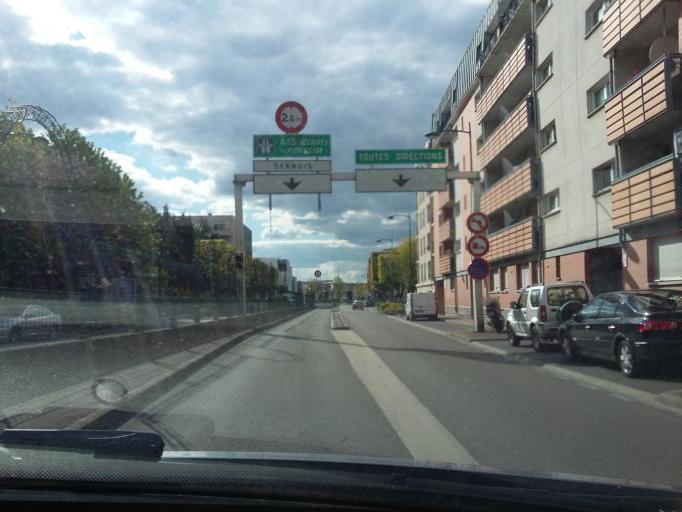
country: FR
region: Ile-de-France
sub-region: Departement du Val-d'Oise
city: Saint-Gratien
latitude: 48.9649
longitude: 2.2861
